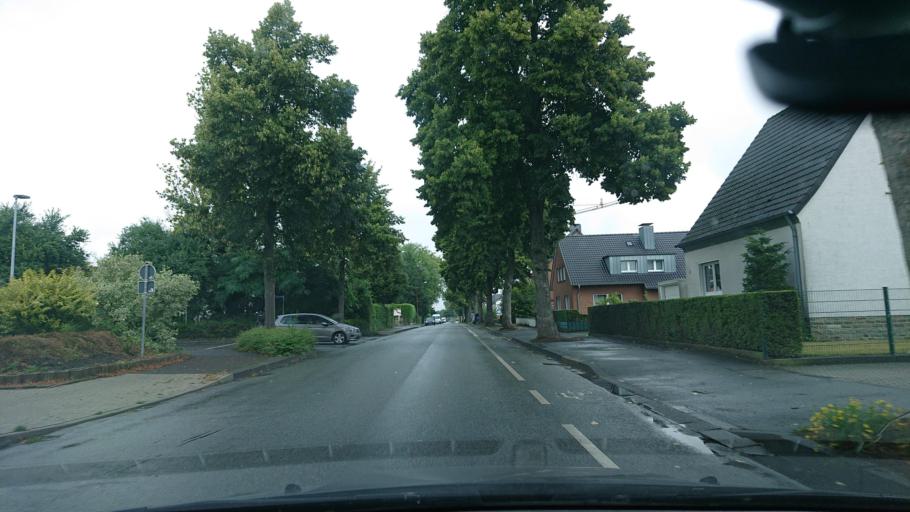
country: DE
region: North Rhine-Westphalia
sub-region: Regierungsbezirk Arnsberg
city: Soest
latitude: 51.5822
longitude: 8.1120
